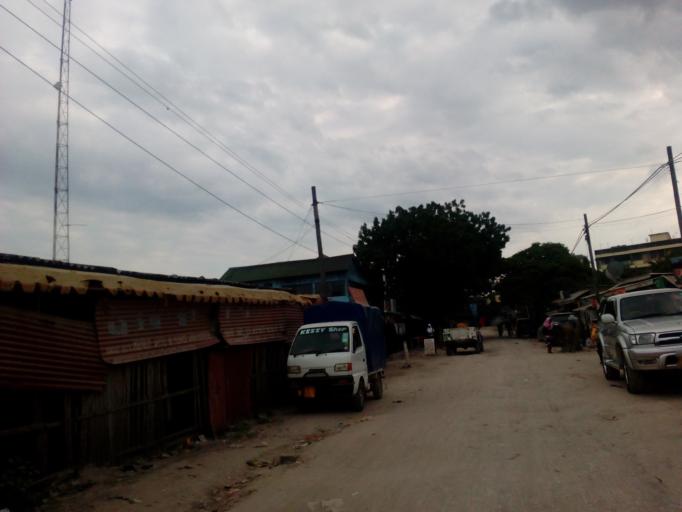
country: TZ
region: Dar es Salaam
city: Dar es Salaam
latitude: -6.8433
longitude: 39.2750
